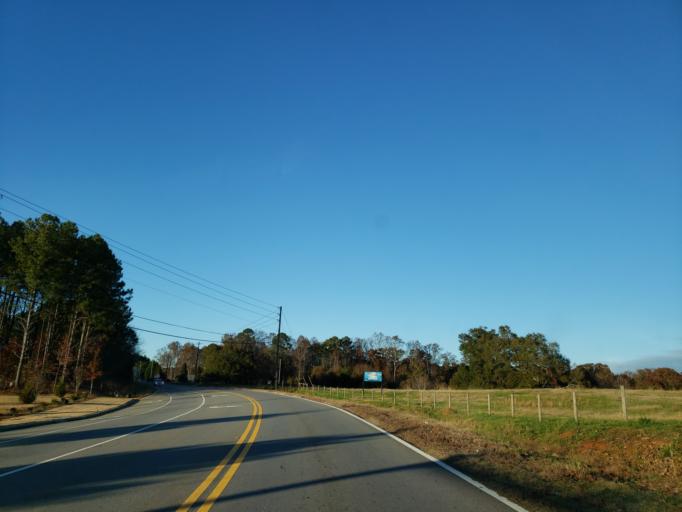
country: US
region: Georgia
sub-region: Cherokee County
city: Holly Springs
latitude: 34.1792
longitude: -84.4197
